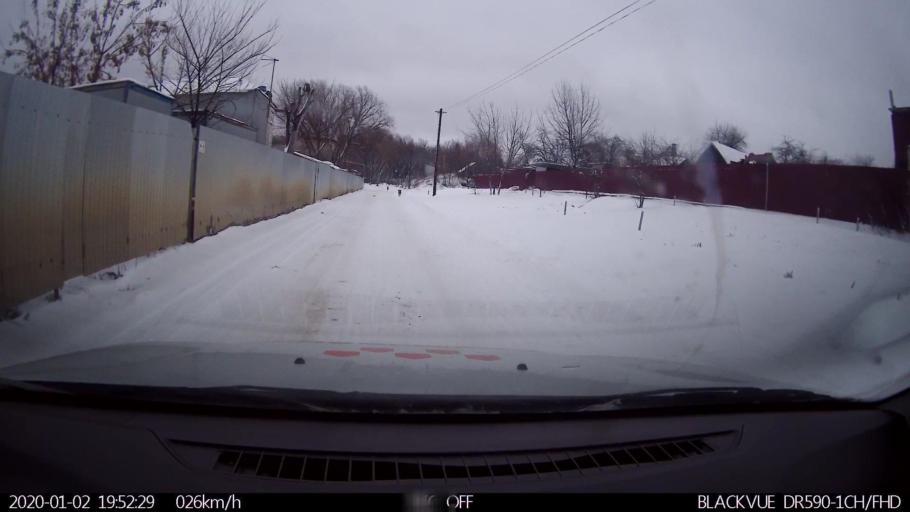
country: RU
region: Nizjnij Novgorod
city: Nizhniy Novgorod
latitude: 56.2729
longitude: 43.9566
